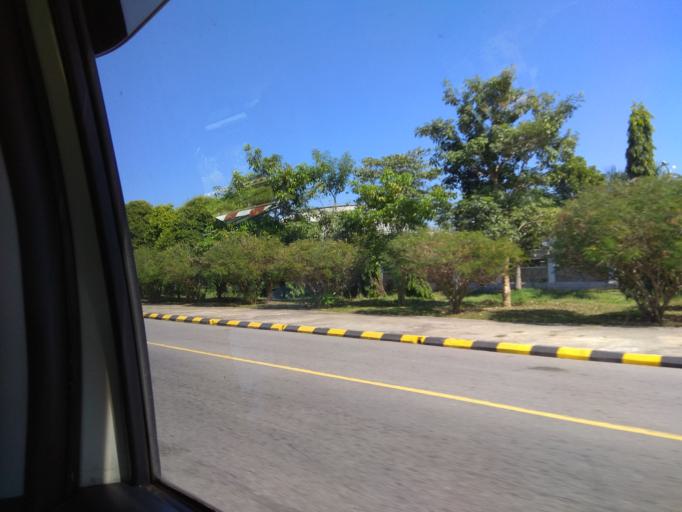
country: MM
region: Mandalay
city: Nay Pyi Taw
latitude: 19.7394
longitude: 96.1135
